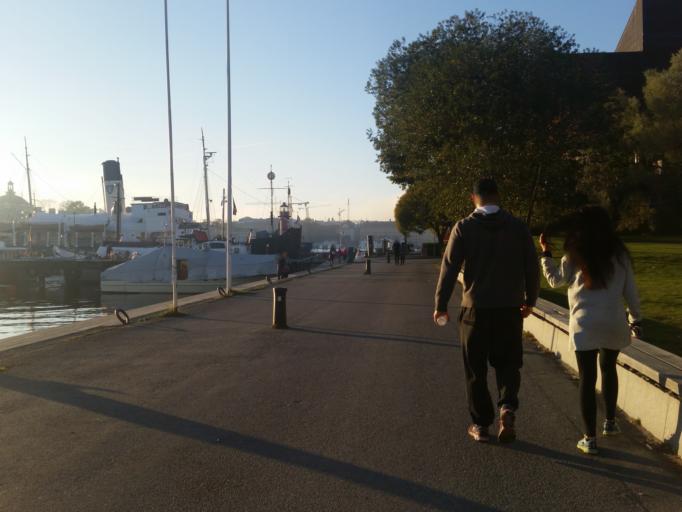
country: SE
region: Stockholm
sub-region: Stockholms Kommun
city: OEstermalm
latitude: 59.3271
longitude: 18.0931
